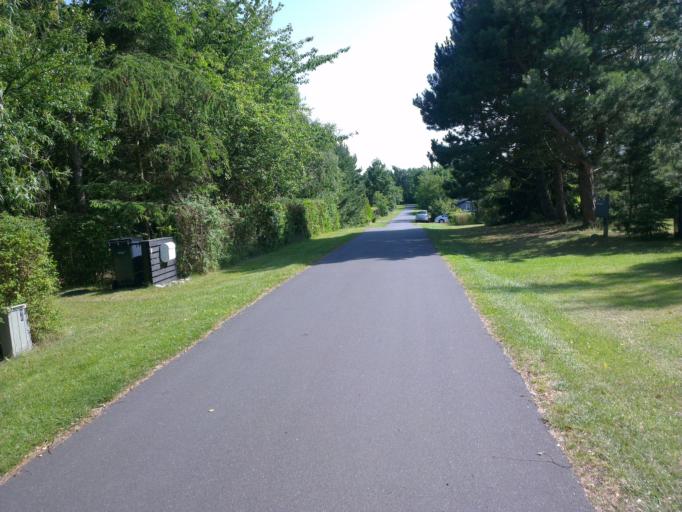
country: DK
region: Capital Region
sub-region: Halsnaes Kommune
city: Hundested
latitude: 55.9250
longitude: 11.9110
